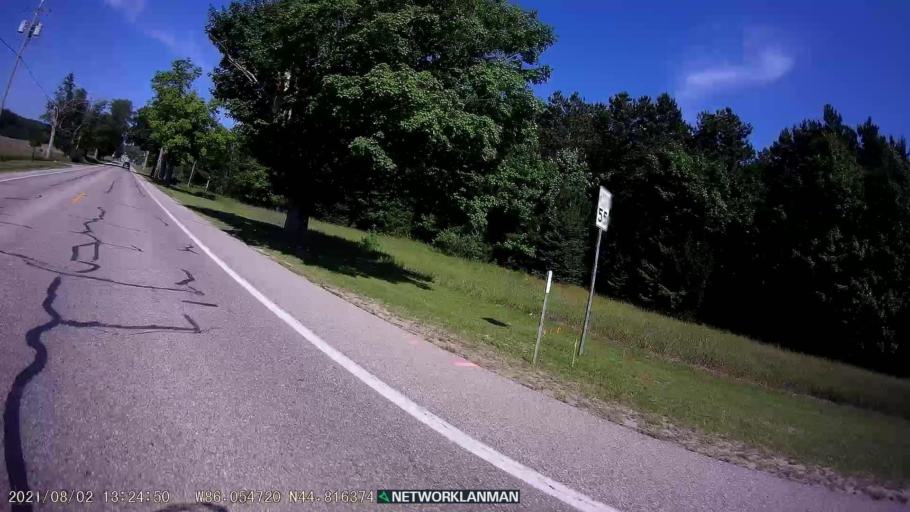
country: US
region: Michigan
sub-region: Benzie County
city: Beulah
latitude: 44.8166
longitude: -86.0544
